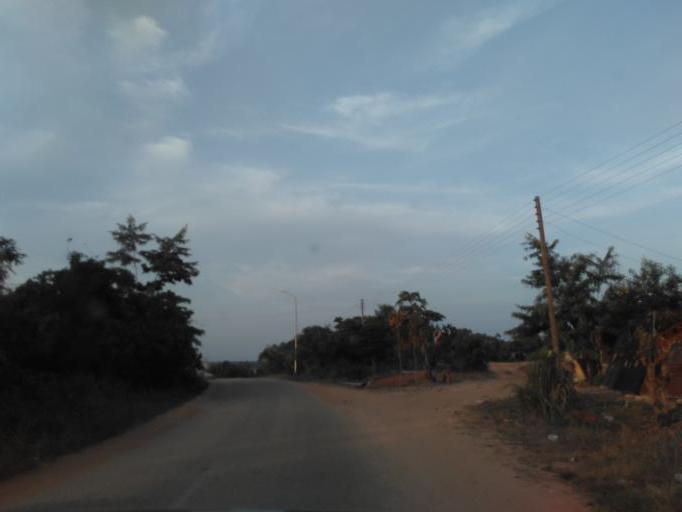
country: GH
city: Bekwai
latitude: 6.5398
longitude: -1.4712
